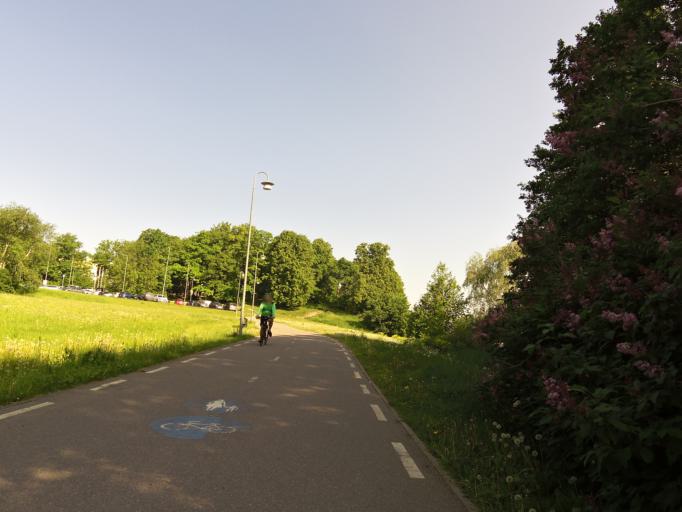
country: EE
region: Harju
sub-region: Saue vald
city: Laagri
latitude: 59.4298
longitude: 24.6530
